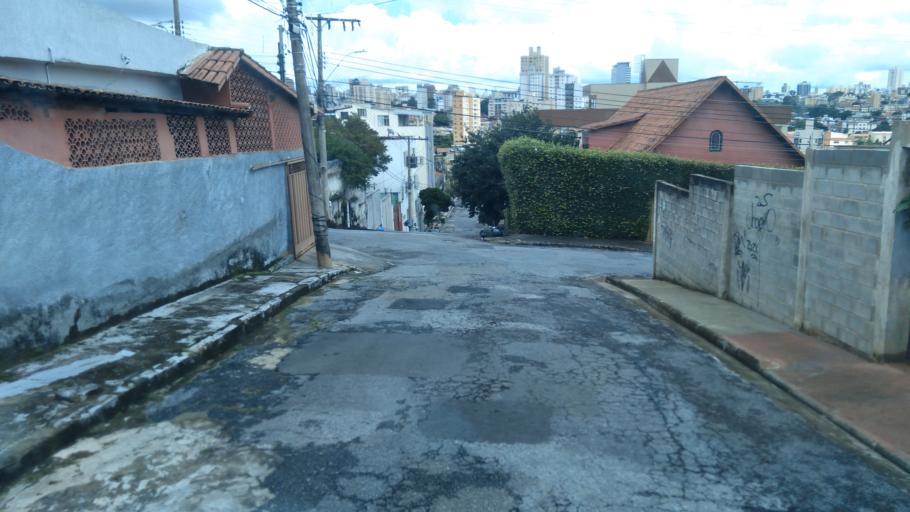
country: BR
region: Minas Gerais
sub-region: Belo Horizonte
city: Belo Horizonte
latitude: -19.9211
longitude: -43.9085
